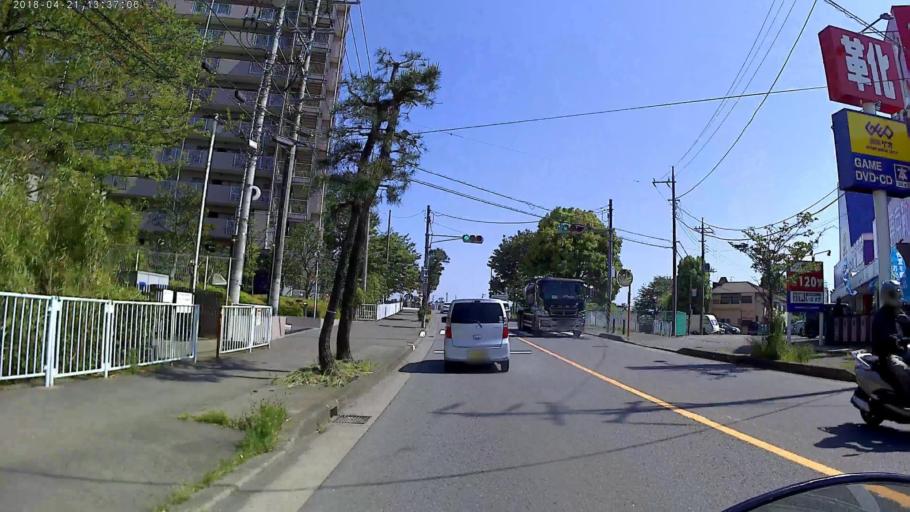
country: JP
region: Kanagawa
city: Atsugi
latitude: 35.3840
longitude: 139.3823
